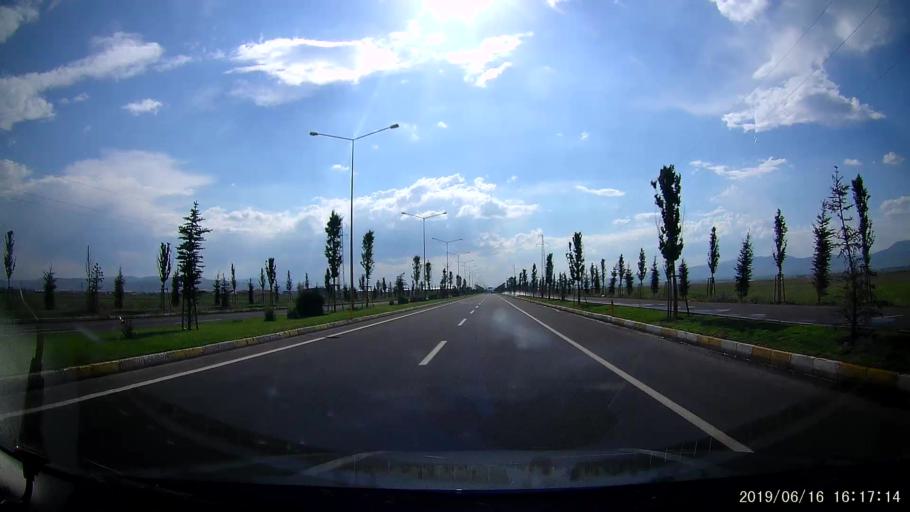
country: TR
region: Erzurum
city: Ilica
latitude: 39.9637
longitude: 41.1916
